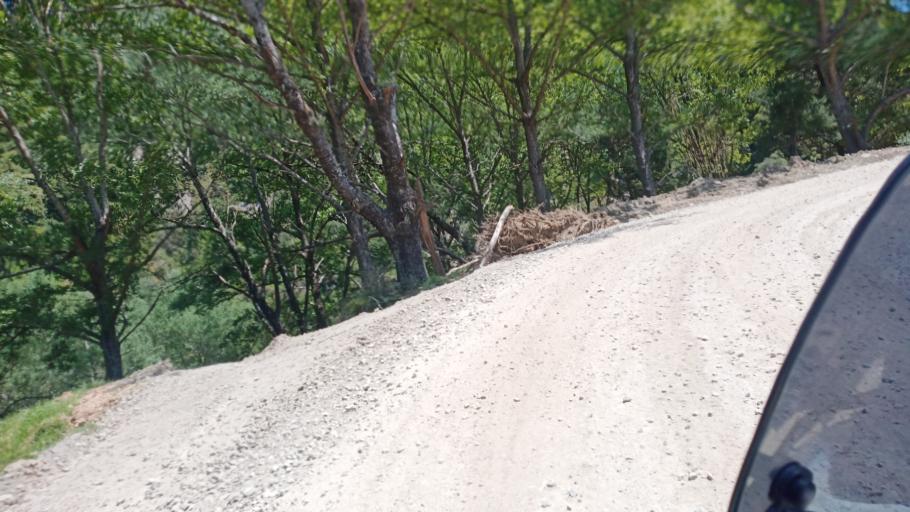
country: NZ
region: Gisborne
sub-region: Gisborne District
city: Gisborne
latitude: -38.2831
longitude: 177.9976
